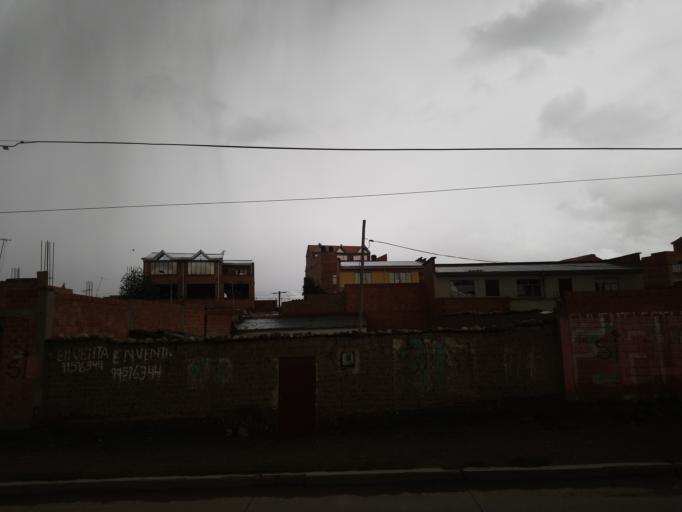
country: BO
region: La Paz
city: La Paz
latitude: -16.5107
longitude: -68.2069
